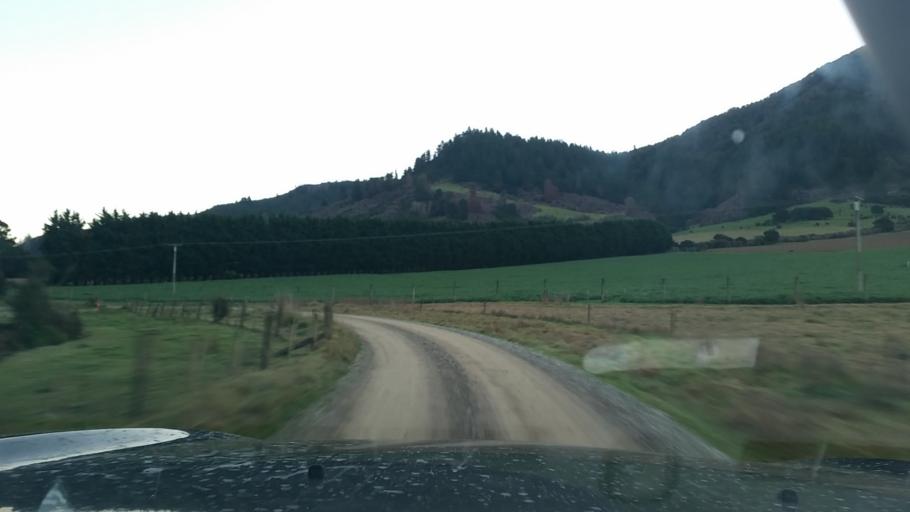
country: NZ
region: Marlborough
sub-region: Marlborough District
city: Picton
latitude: -41.1455
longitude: 174.1345
